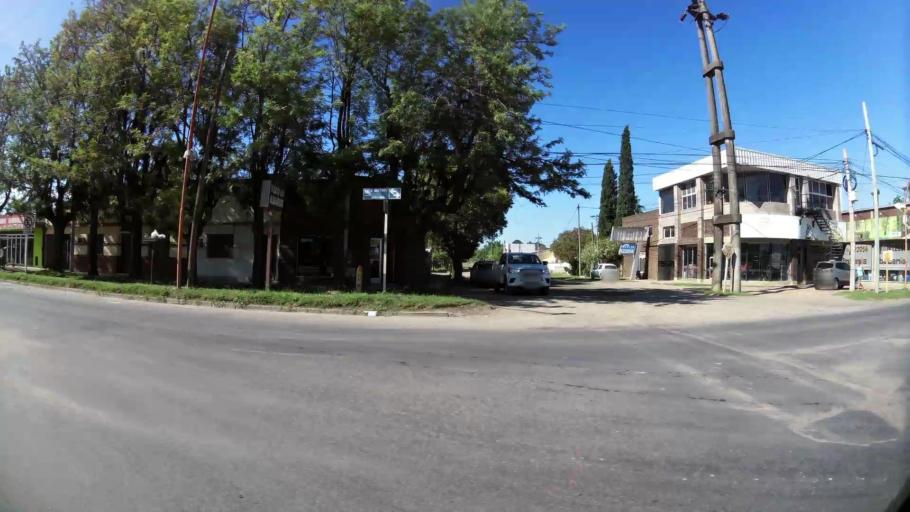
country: AR
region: Santa Fe
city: Esperanza
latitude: -31.4458
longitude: -60.9157
